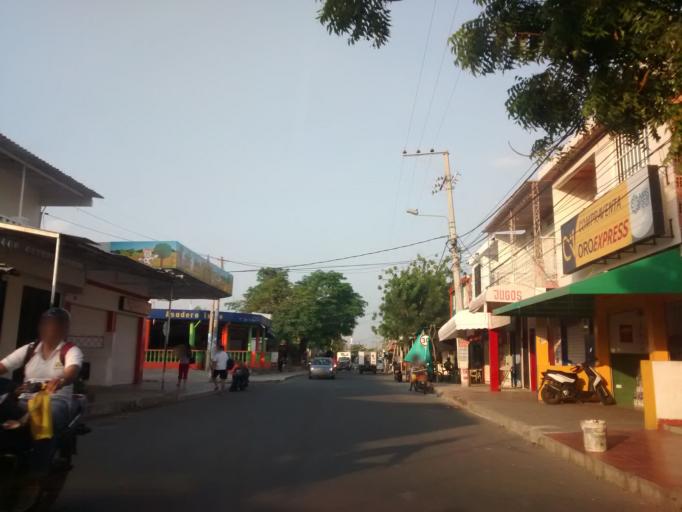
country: CO
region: Cundinamarca
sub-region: Girardot
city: Girardot City
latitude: 4.3123
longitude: -74.7893
